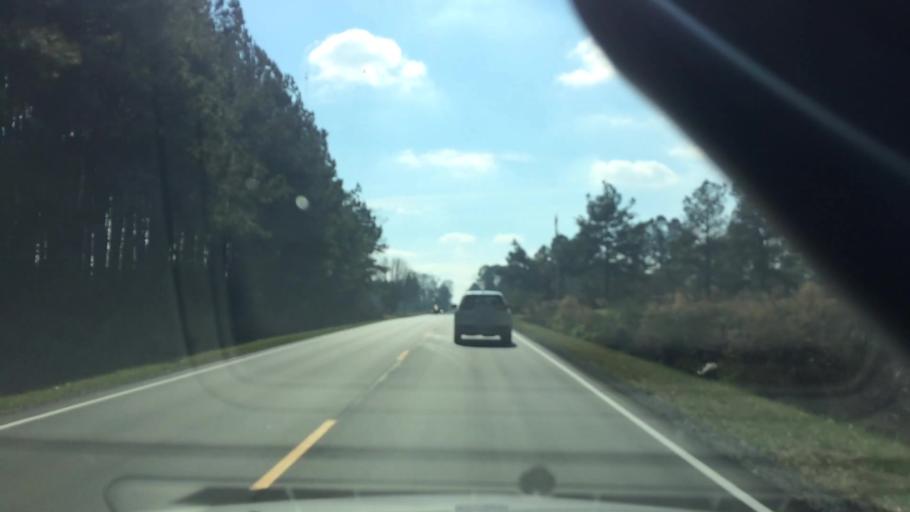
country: US
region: North Carolina
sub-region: Duplin County
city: Beulaville
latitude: 34.9388
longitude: -77.7699
